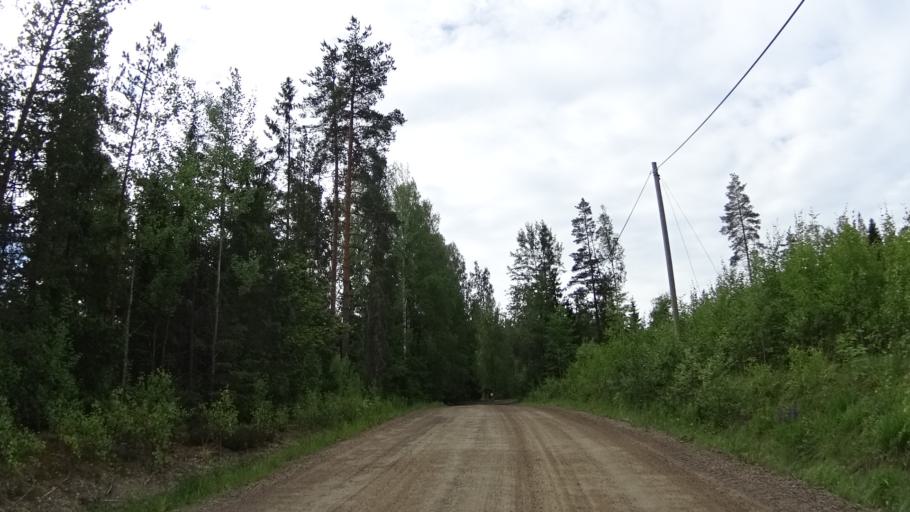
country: FI
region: Uusimaa
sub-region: Helsinki
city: Karkkila
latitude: 60.5027
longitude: 24.2649
